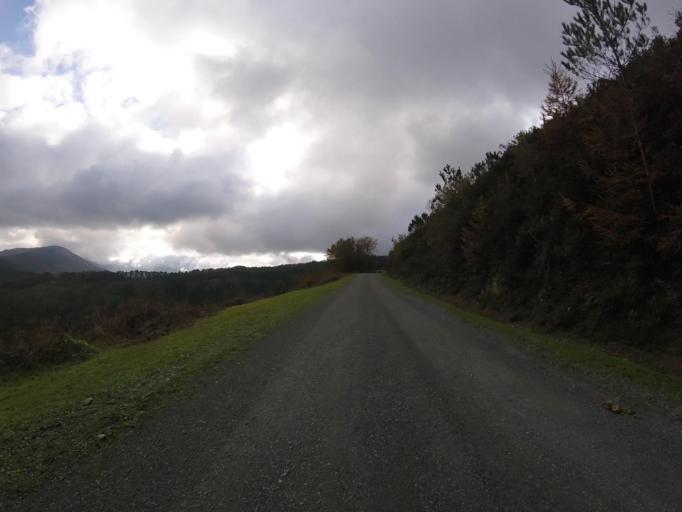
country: ES
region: Navarre
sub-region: Provincia de Navarra
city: Goizueta
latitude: 43.2160
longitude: -1.8205
